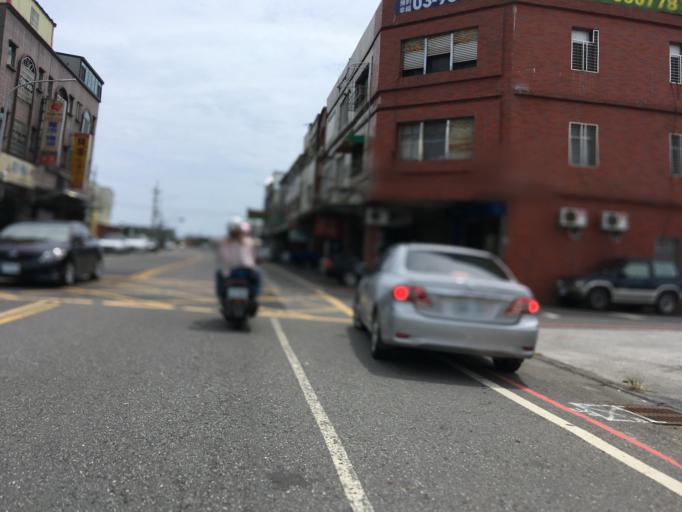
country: TW
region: Taiwan
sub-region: Yilan
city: Yilan
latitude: 24.6859
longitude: 121.8003
